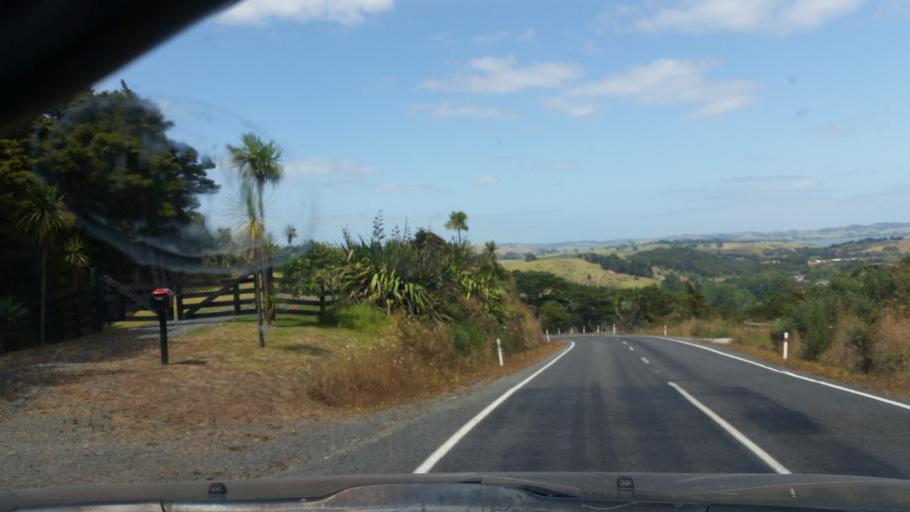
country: NZ
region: Northland
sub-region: Whangarei
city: Ruakaka
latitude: -36.0879
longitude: 174.2396
